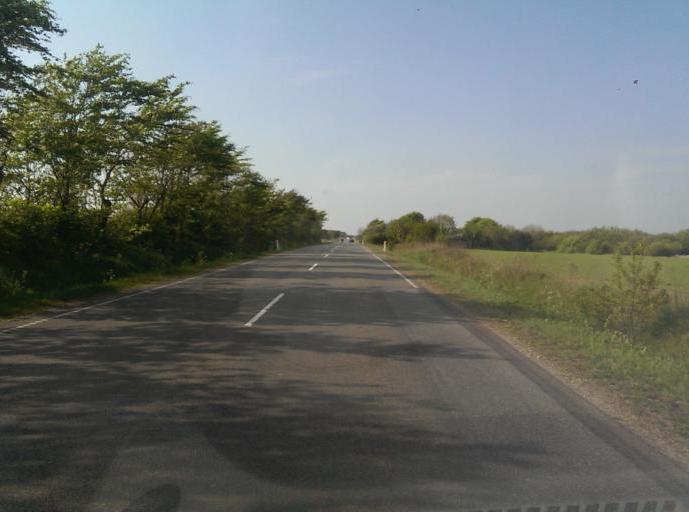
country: DK
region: South Denmark
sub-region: Esbjerg Kommune
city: Tjaereborg
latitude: 55.5119
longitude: 8.5946
